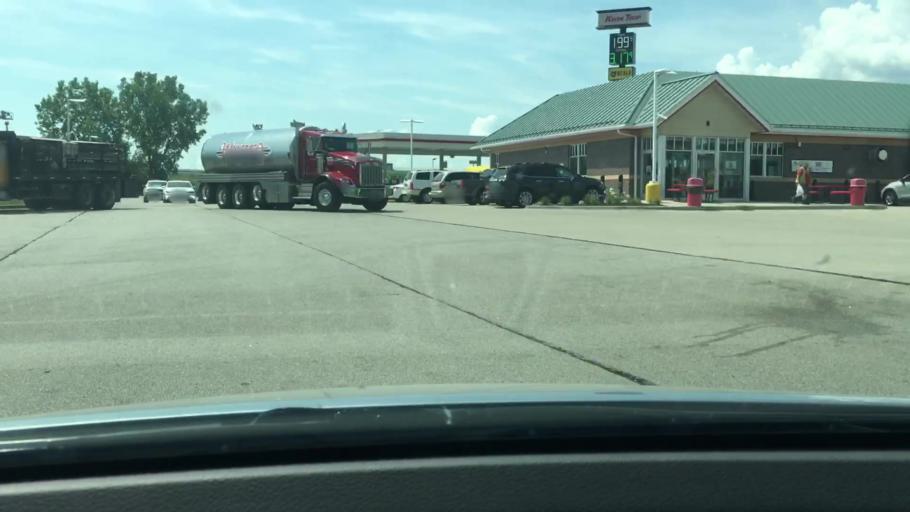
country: US
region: Wisconsin
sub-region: Winnebago County
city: Oshkosh
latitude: 44.1005
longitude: -88.5421
